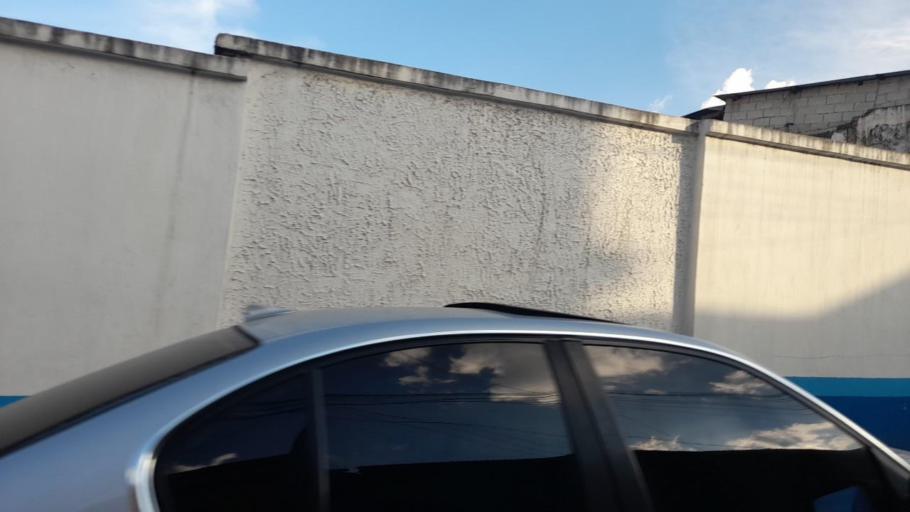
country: GT
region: Quetzaltenango
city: Quetzaltenango
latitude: 14.8357
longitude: -91.5145
